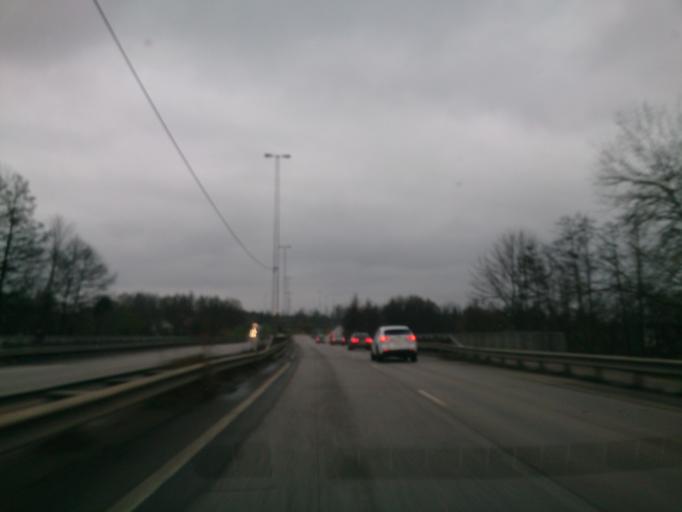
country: SE
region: OEstergoetland
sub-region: Norrkopings Kommun
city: Norrkoping
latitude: 58.5884
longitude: 16.1517
